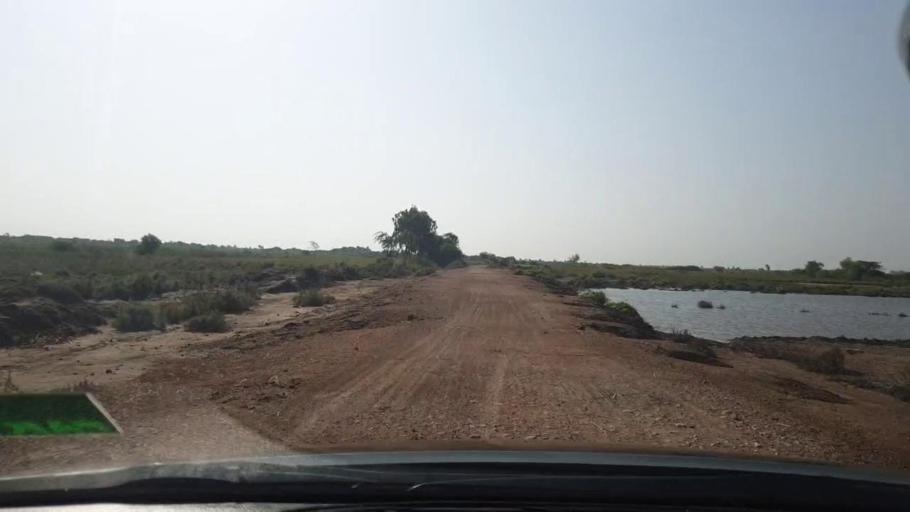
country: PK
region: Sindh
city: Tando Bago
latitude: 24.7171
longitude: 68.9689
